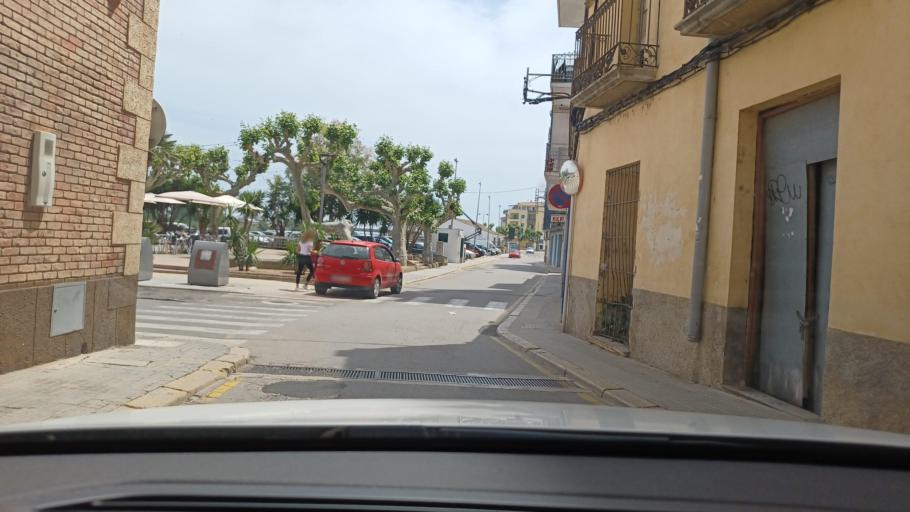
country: ES
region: Catalonia
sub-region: Provincia de Tarragona
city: Amposta
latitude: 40.7135
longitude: 0.5821
